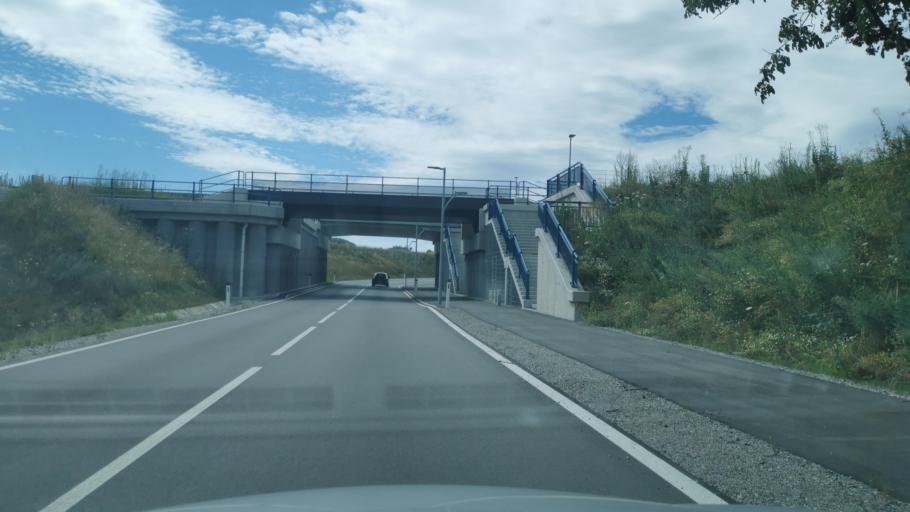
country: AT
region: Lower Austria
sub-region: Politischer Bezirk Sankt Polten
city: Wilhelmsburg
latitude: 48.1310
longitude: 15.6137
